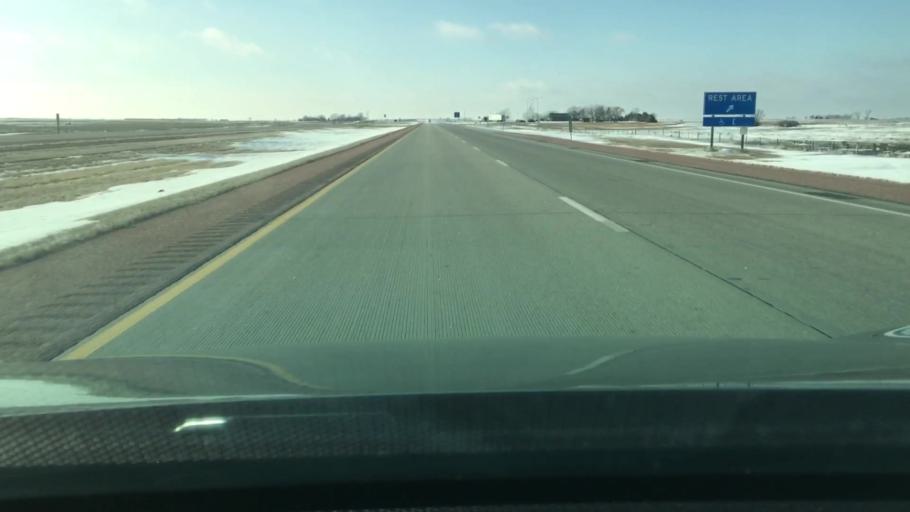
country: US
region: South Dakota
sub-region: Aurora County
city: Plankinton
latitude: 43.7084
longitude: -98.6091
